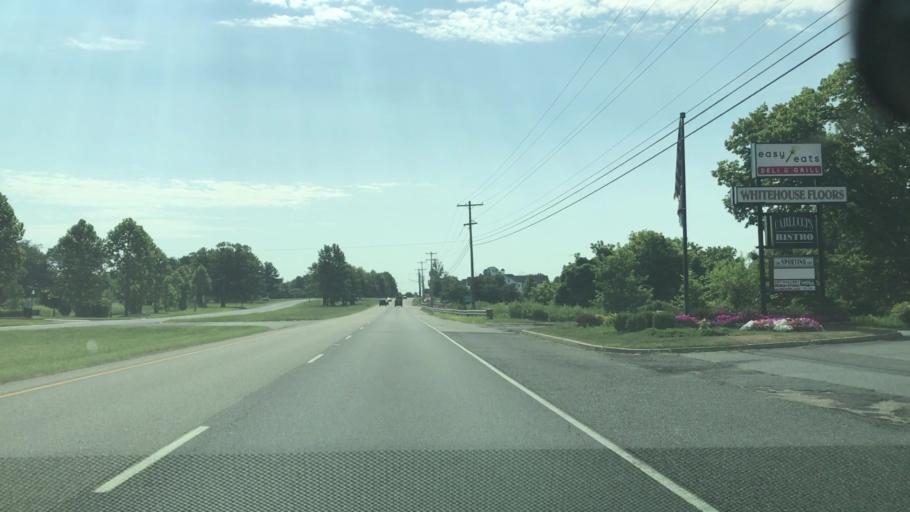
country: US
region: New Jersey
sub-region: Hunterdon County
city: Whitehouse Station
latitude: 40.6177
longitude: -74.7455
